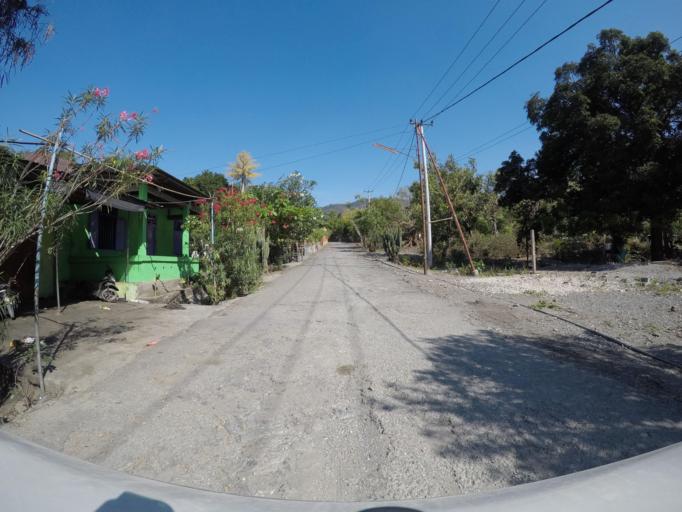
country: TL
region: Liquica
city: Maubara
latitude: -8.6149
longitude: 125.2072
